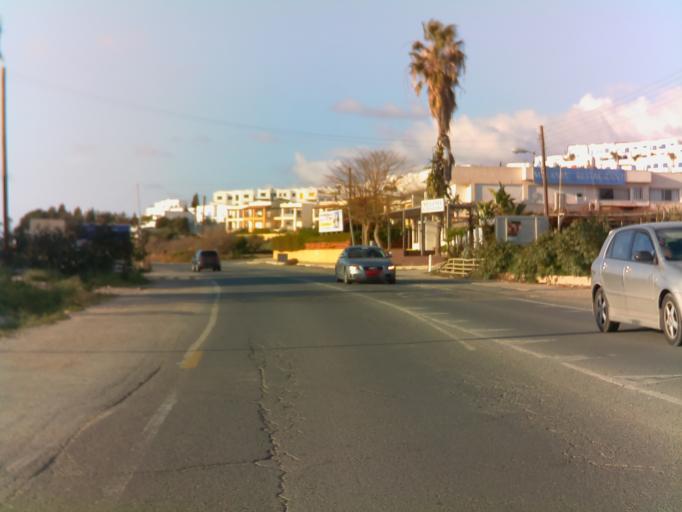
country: CY
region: Pafos
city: Chlorakas
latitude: 34.7860
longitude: 32.4055
